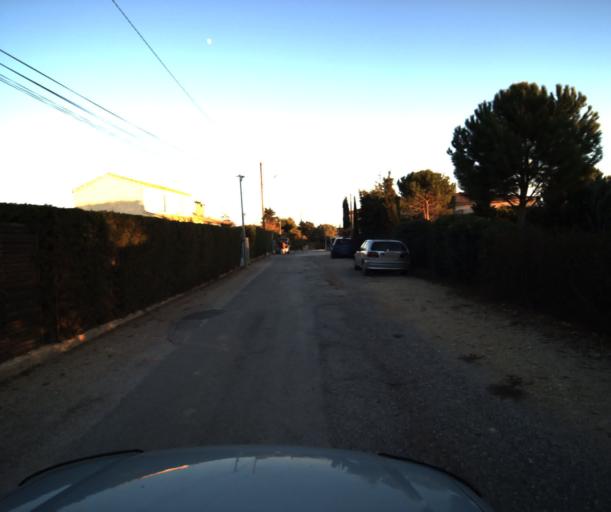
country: FR
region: Provence-Alpes-Cote d'Azur
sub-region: Departement du Vaucluse
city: Pertuis
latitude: 43.7039
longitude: 5.4948
